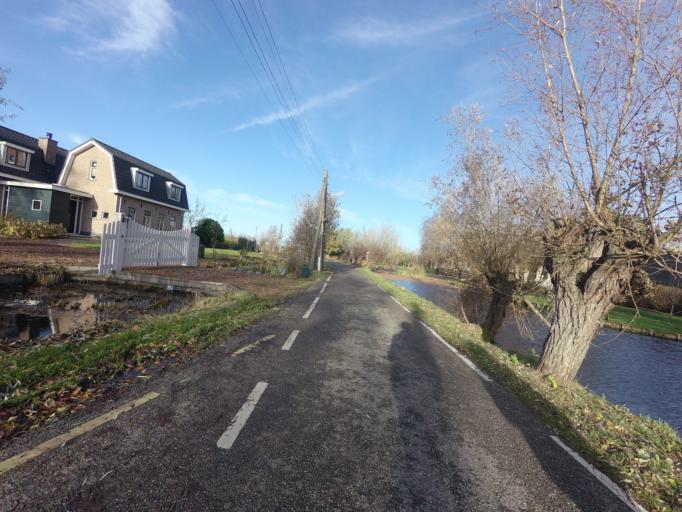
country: NL
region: South Holland
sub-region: Gemeente Vlist
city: Haastrecht
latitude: 52.0340
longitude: 4.7724
